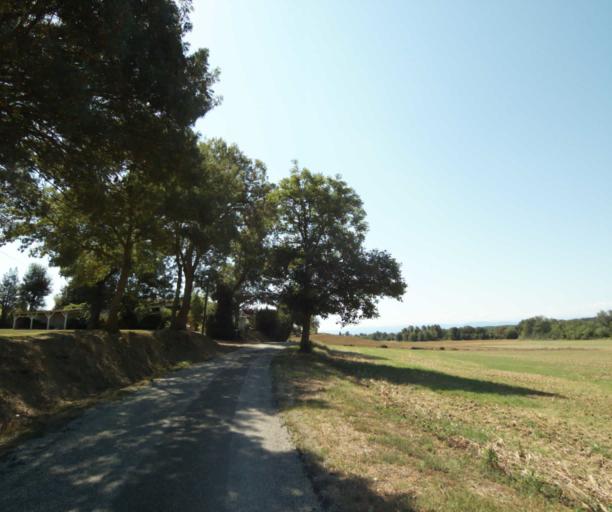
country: FR
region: Midi-Pyrenees
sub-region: Departement de l'Ariege
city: Lezat-sur-Leze
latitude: 43.2604
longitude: 1.3663
